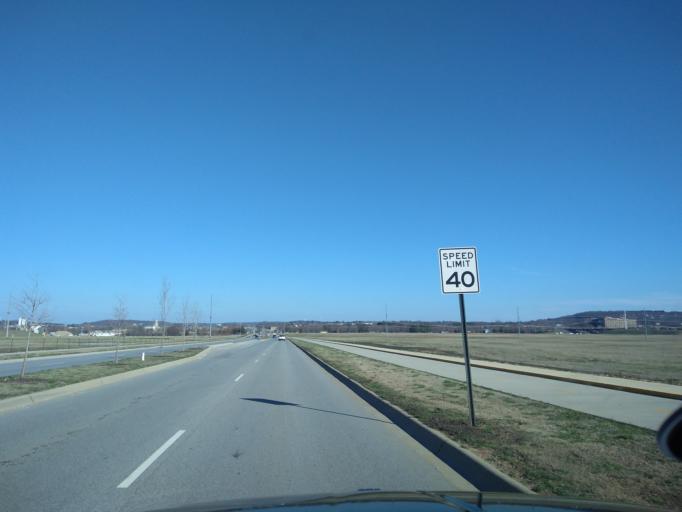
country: US
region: Arkansas
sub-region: Washington County
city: Johnson
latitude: 36.1172
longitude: -94.1734
